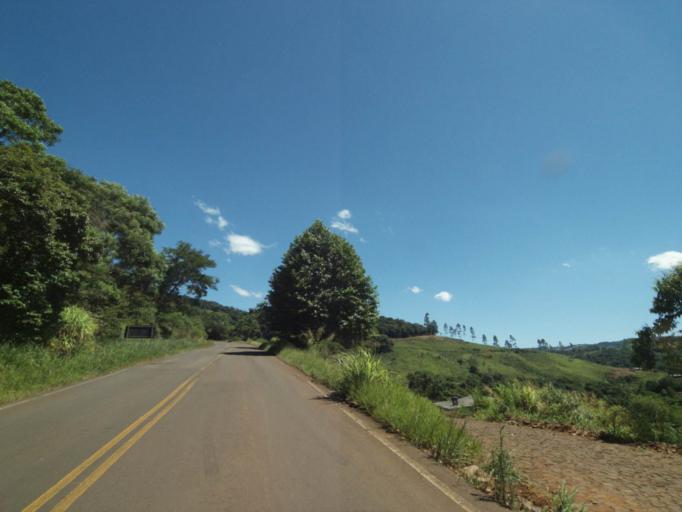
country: BR
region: Parana
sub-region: Ampere
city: Ampere
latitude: -26.1825
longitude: -53.3642
